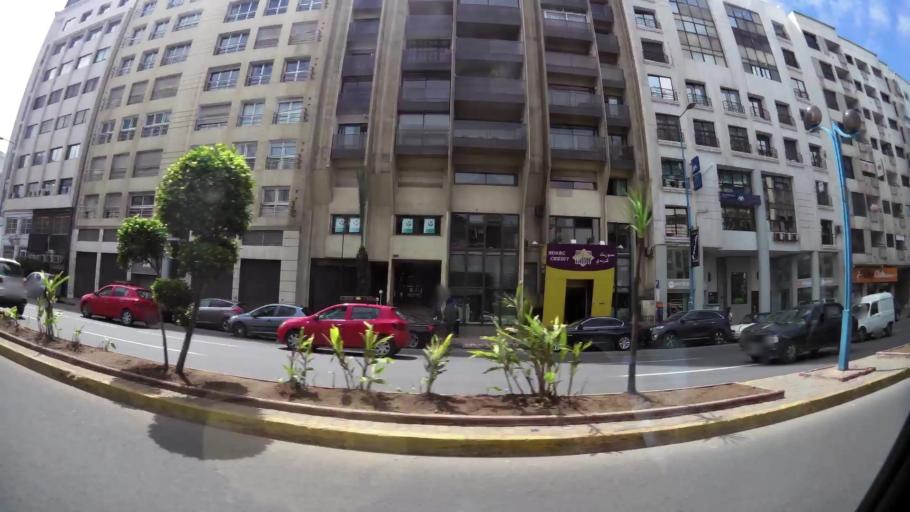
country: MA
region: Grand Casablanca
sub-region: Casablanca
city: Casablanca
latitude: 33.5916
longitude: -7.6366
